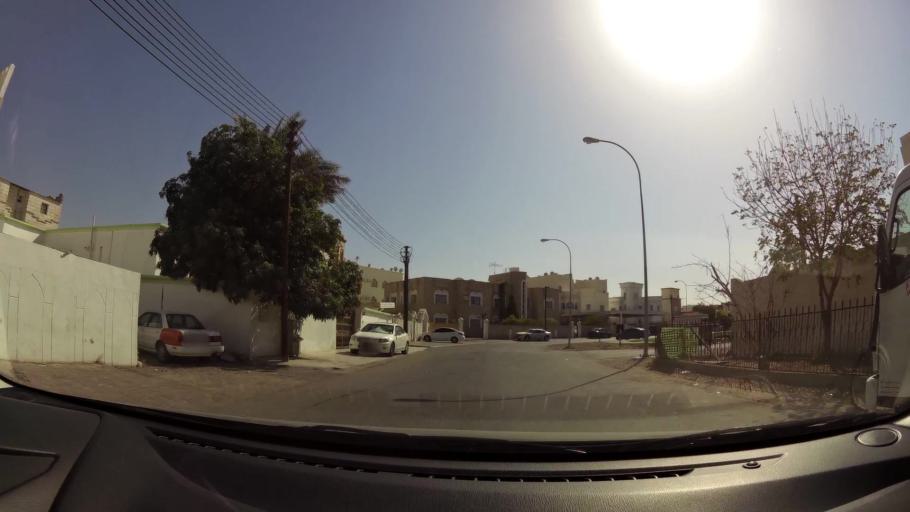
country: OM
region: Muhafazat Masqat
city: As Sib al Jadidah
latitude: 23.6277
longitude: 58.2026
